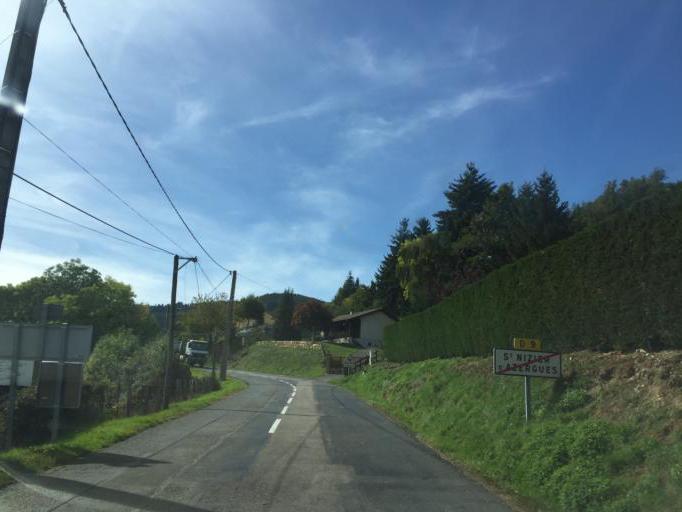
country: FR
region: Rhone-Alpes
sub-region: Departement du Rhone
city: Grandris
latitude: 46.0860
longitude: 4.4626
